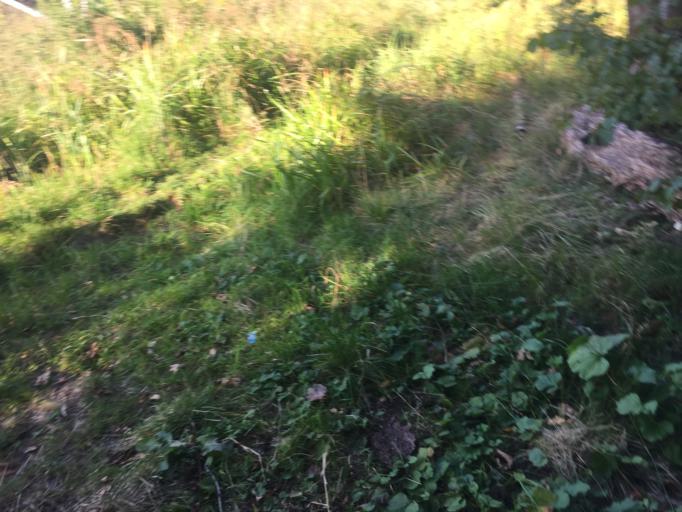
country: RU
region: Moscow
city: Metrogorodok
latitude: 55.8470
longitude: 37.7702
